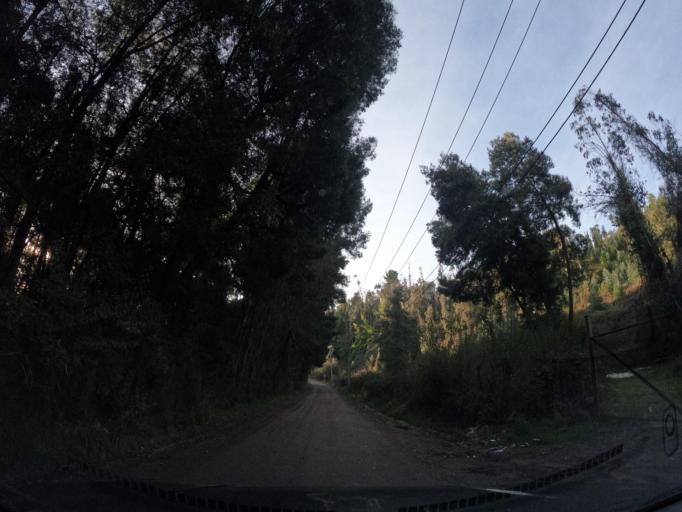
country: CL
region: Biobio
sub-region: Provincia de Concepcion
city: Chiguayante
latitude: -36.8693
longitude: -72.9954
